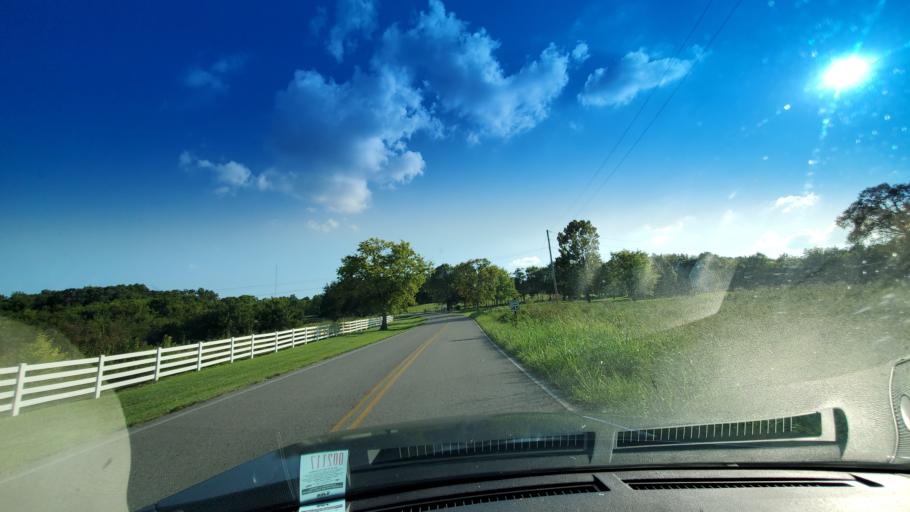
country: US
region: Tennessee
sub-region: Wilson County
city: Lebanon
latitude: 36.1624
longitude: -86.3741
